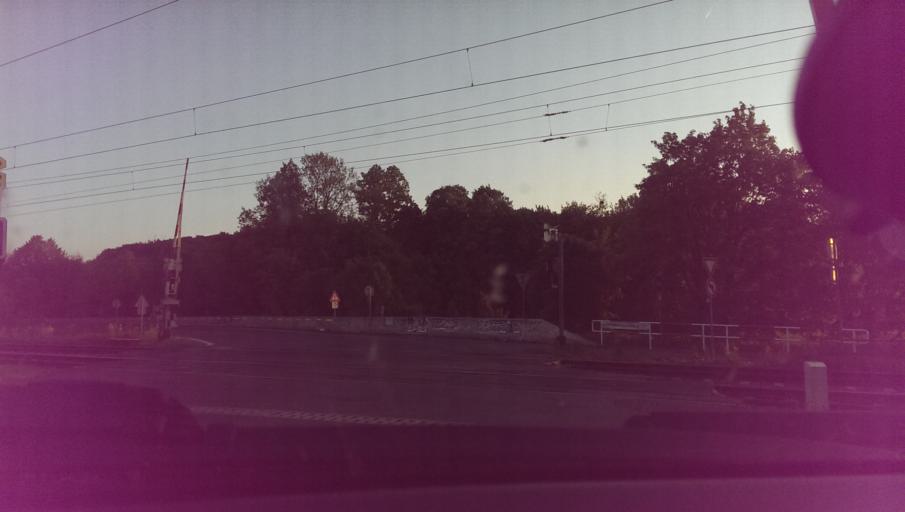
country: CZ
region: Zlin
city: Valasske Mezirici
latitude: 49.4520
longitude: 17.9692
